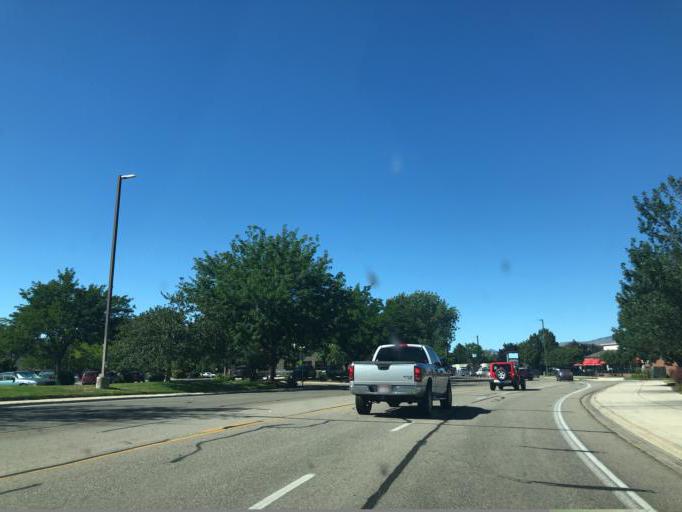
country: US
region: Idaho
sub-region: Ada County
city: Garden City
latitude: 43.6097
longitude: -116.2846
